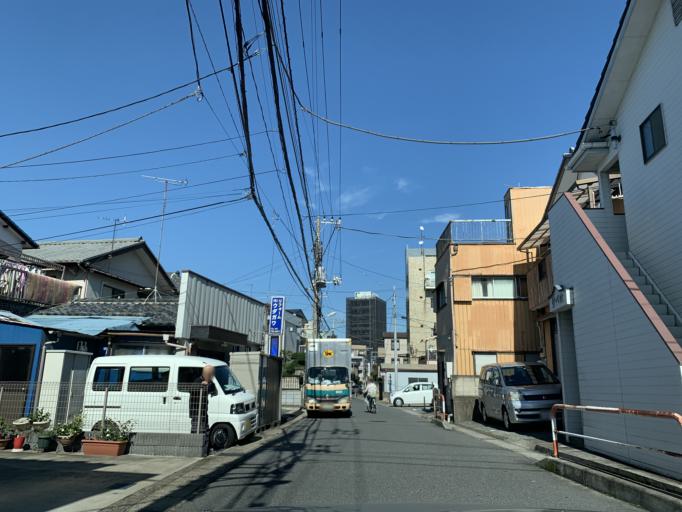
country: JP
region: Tokyo
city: Urayasu
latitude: 35.6623
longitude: 139.8955
